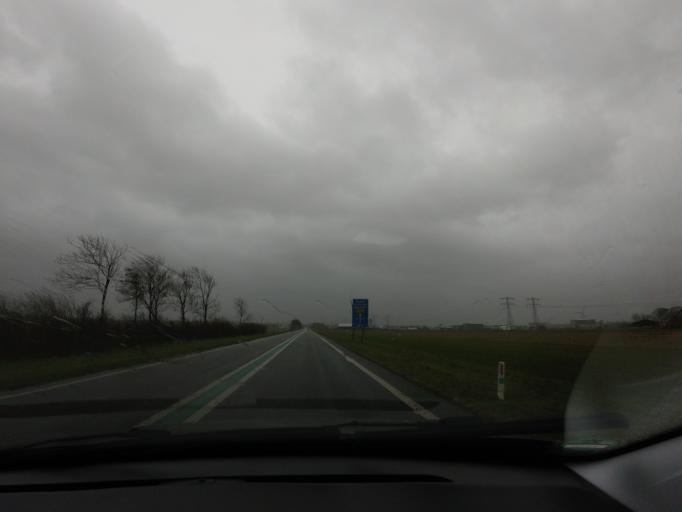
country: NL
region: Friesland
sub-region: Sudwest Fryslan
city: Bolsward
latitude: 53.0722
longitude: 5.5105
